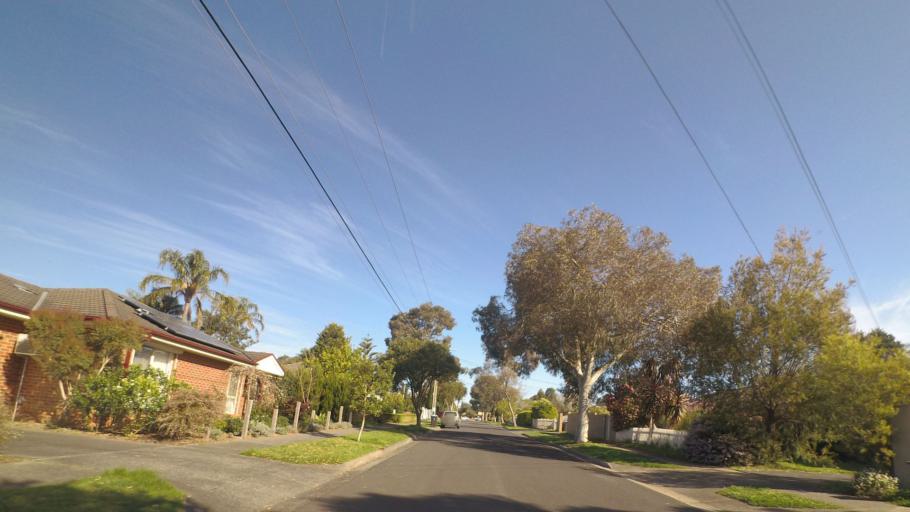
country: AU
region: Victoria
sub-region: Maroondah
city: Heathmont
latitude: -37.8405
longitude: 145.2551
